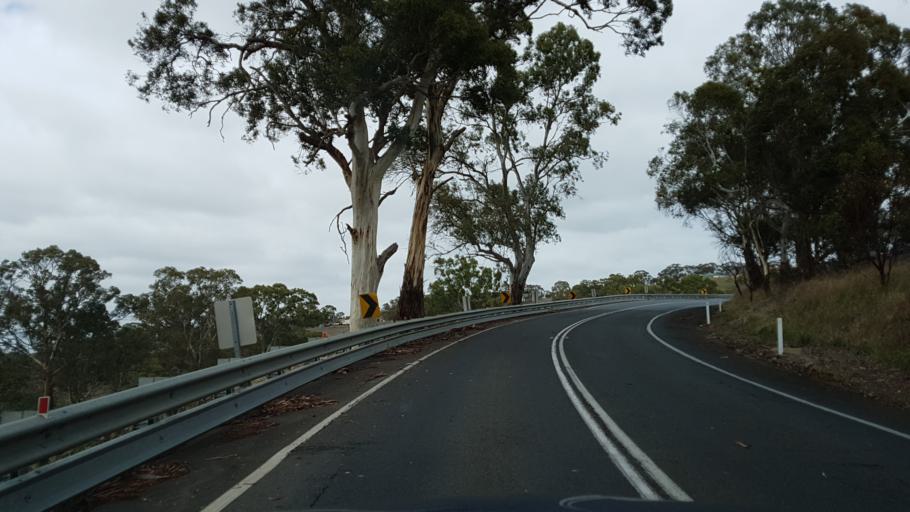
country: AU
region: South Australia
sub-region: Mount Barker
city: Nairne
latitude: -35.0429
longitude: 138.9451
